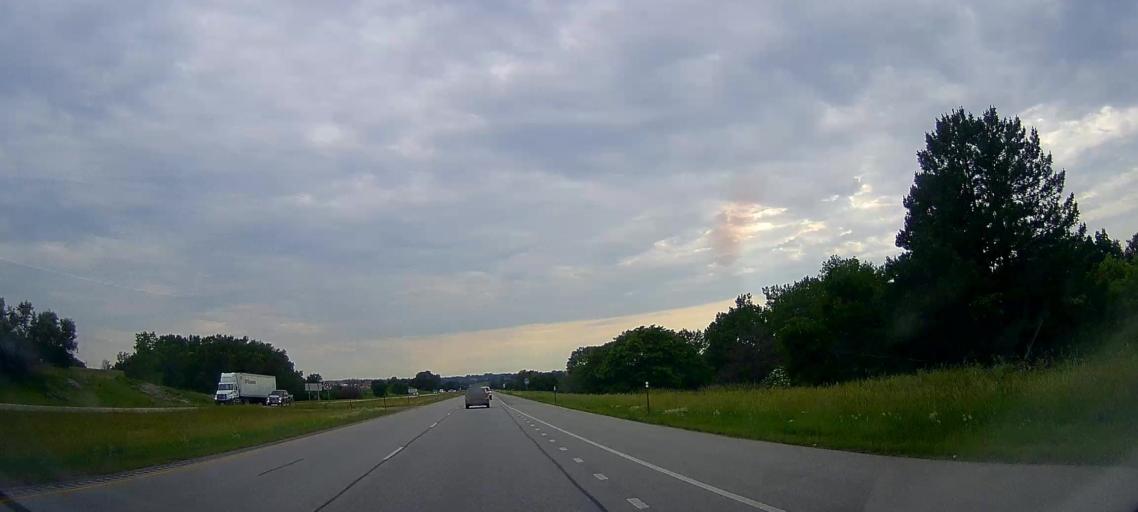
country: US
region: Iowa
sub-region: Pottawattamie County
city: Carter Lake
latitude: 41.3393
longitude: -96.0310
